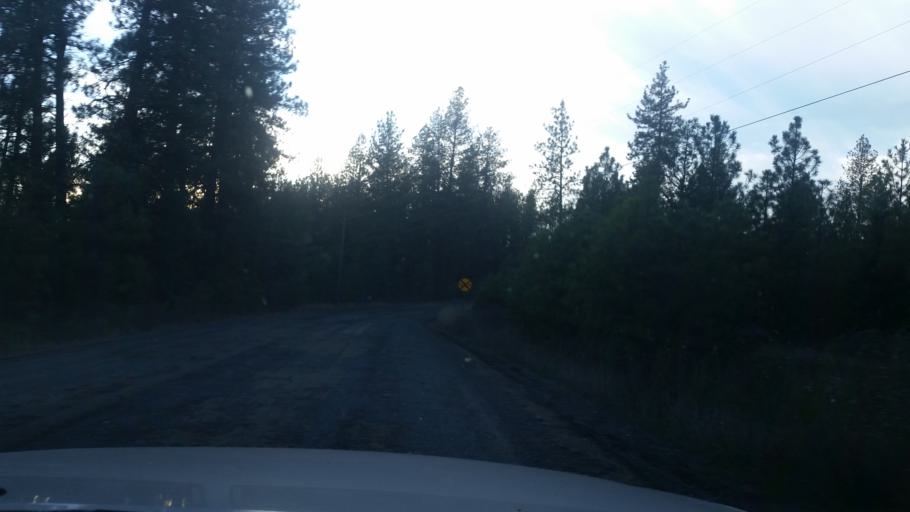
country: US
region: Washington
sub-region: Spokane County
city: Cheney
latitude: 47.5051
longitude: -117.5396
